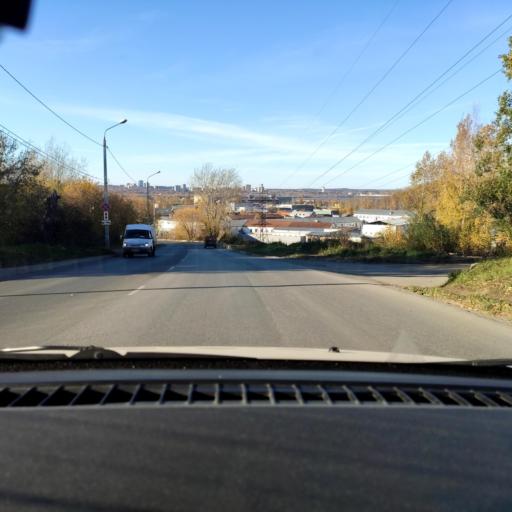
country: RU
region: Perm
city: Perm
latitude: 58.0699
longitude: 56.3537
